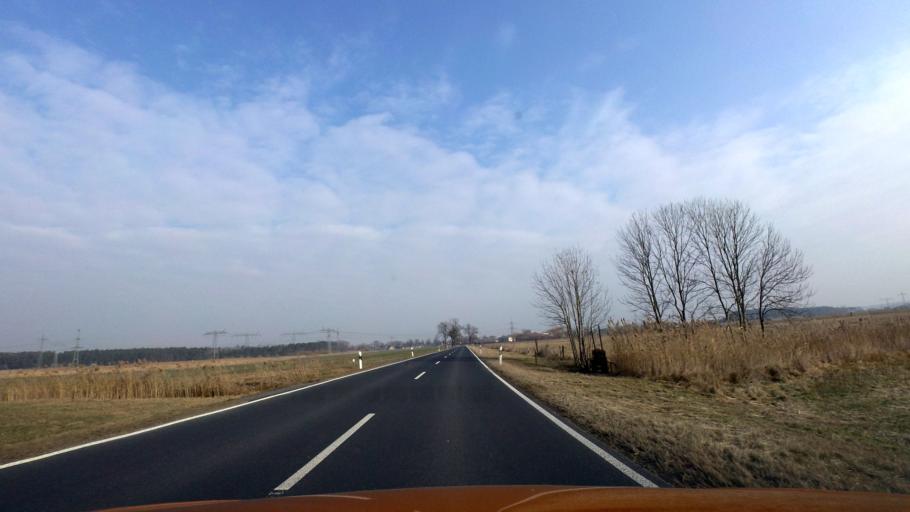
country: DE
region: Brandenburg
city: Trebbin
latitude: 52.2204
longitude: 13.3035
